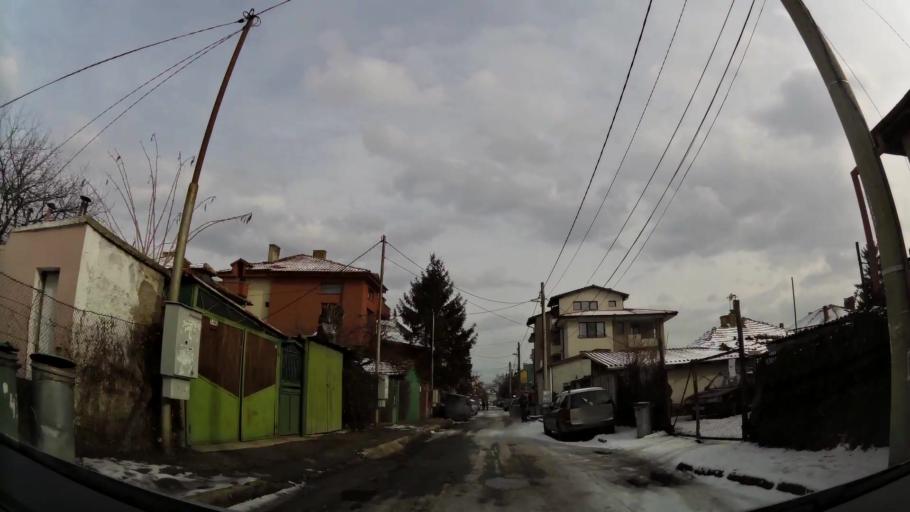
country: BG
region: Sofia-Capital
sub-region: Stolichna Obshtina
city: Sofia
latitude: 42.7054
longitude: 23.3809
